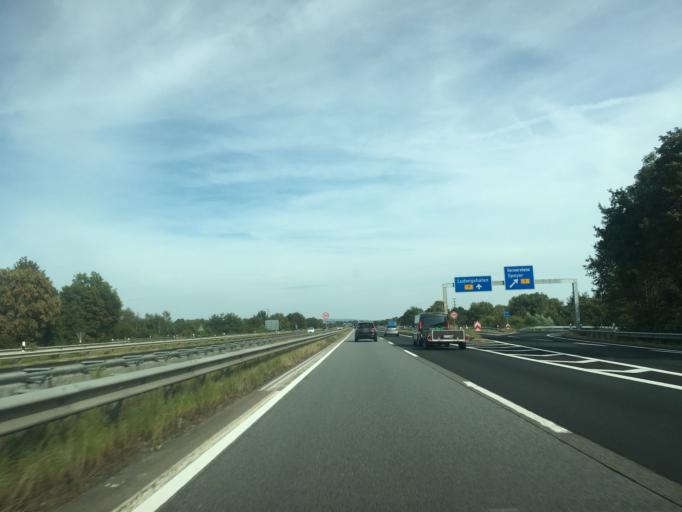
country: DE
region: Rheinland-Pfalz
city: Speyer
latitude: 49.3533
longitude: 8.4175
